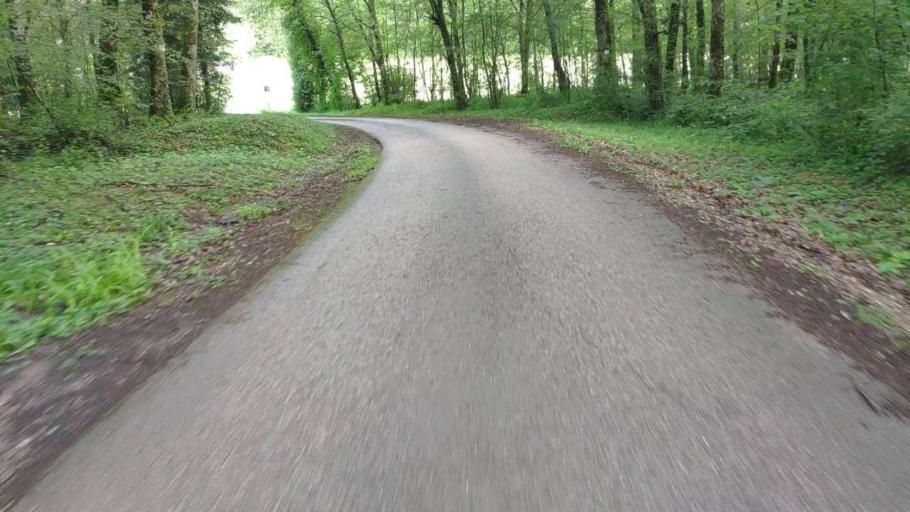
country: FR
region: Franche-Comte
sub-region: Departement du Jura
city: Poligny
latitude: 46.7987
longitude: 5.5981
